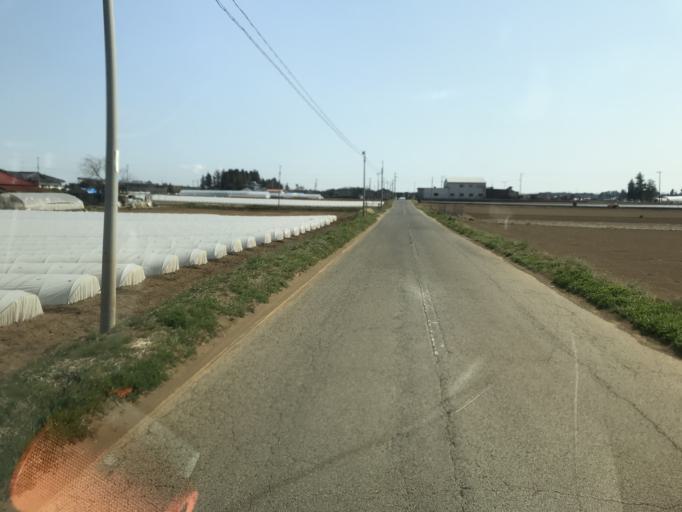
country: JP
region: Chiba
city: Sawara
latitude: 35.8281
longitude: 140.5131
